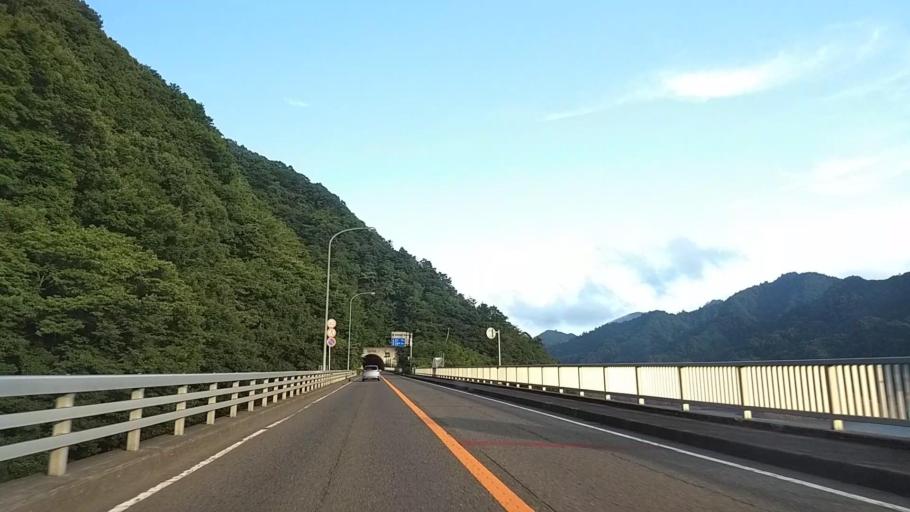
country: JP
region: Kanagawa
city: Atsugi
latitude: 35.5239
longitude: 139.2367
